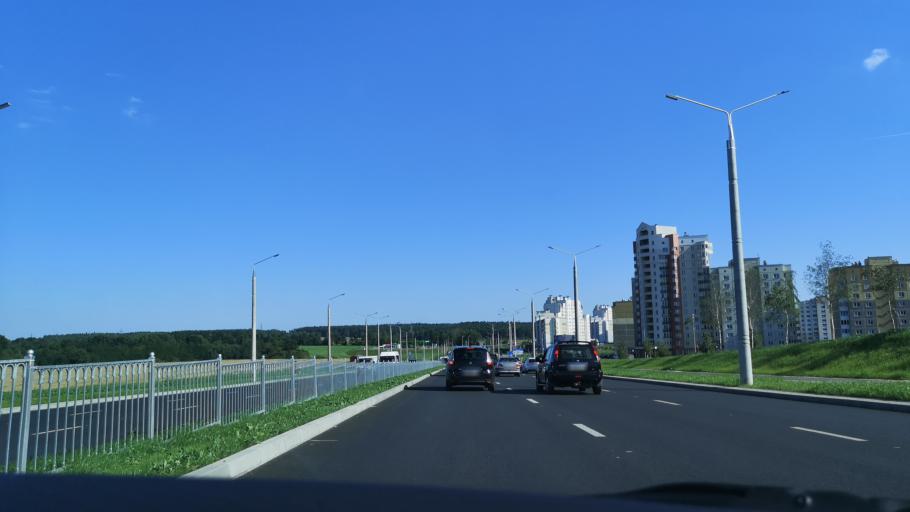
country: BY
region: Grodnenskaya
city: Hrodna
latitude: 53.6485
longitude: 23.8639
